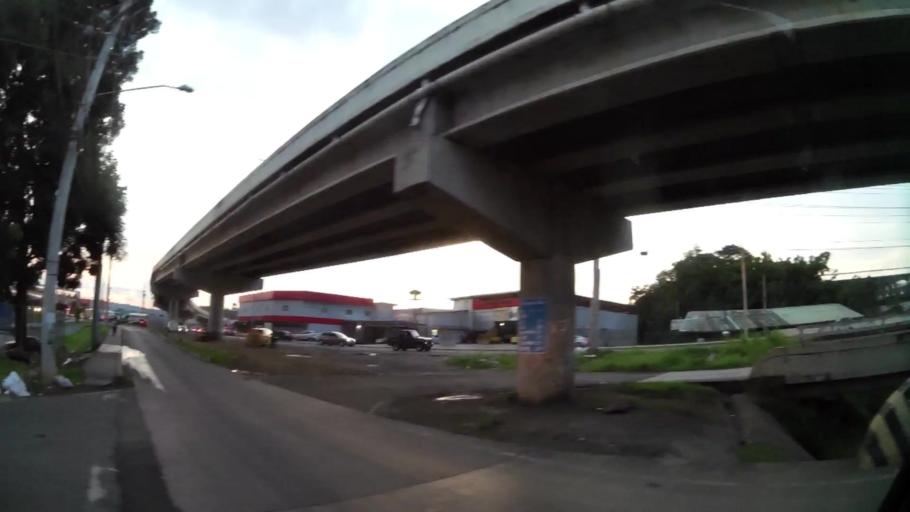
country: PA
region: Panama
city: Tocumen
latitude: 9.0812
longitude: -79.3990
